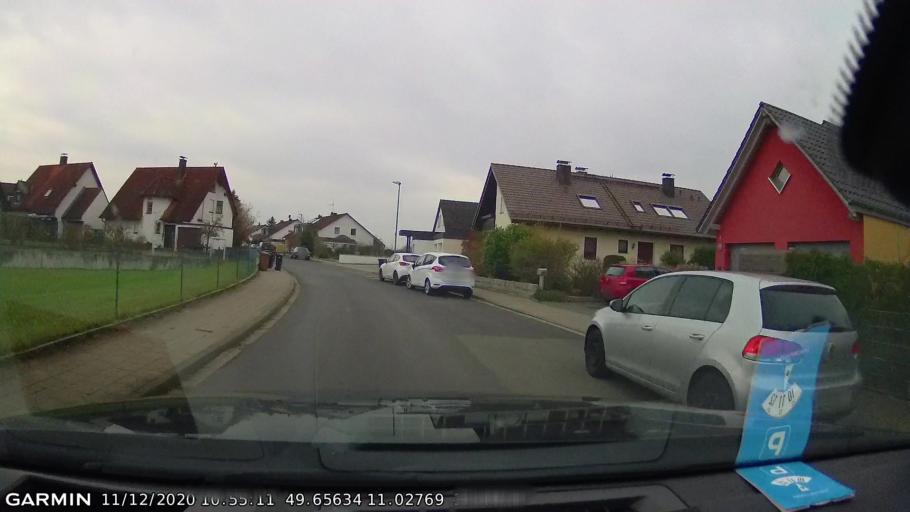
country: DE
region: Bavaria
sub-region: Regierungsbezirk Mittelfranken
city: Baiersdorf
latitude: 49.6563
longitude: 11.0277
